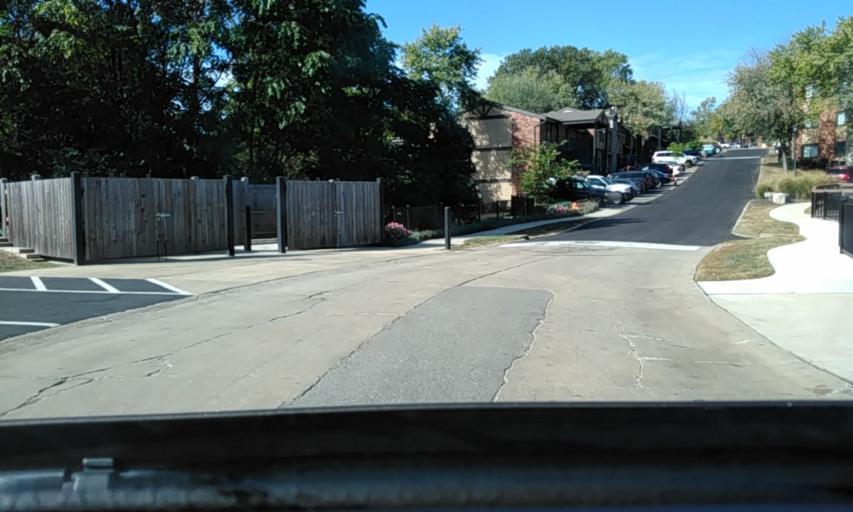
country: US
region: Missouri
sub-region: Saint Louis County
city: Mehlville
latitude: 38.4896
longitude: -90.3488
